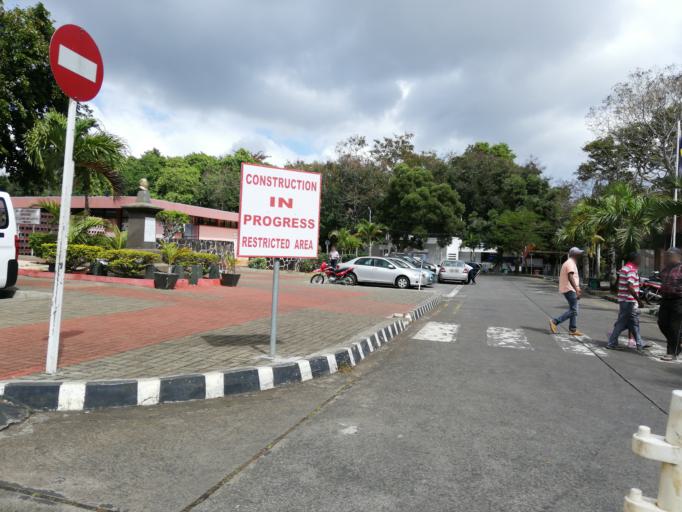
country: MU
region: Pamplemousses
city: Pamplemousses
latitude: -20.0963
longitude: 57.5588
